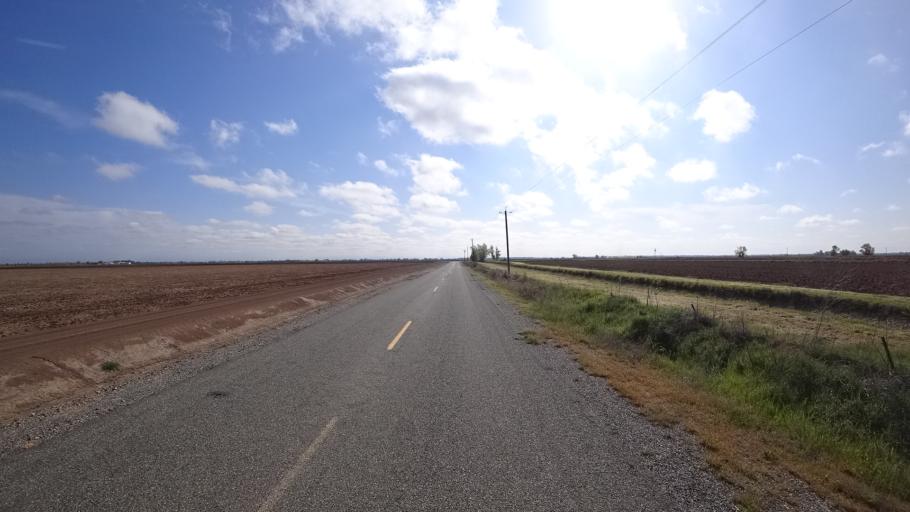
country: US
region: California
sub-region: Butte County
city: Durham
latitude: 39.5224
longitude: -121.9339
